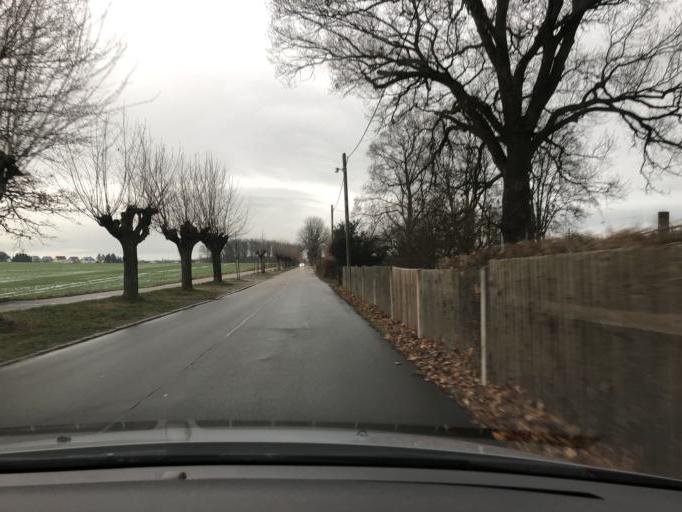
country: DE
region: Saxony
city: Limbach-Oberfrohna
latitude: 50.8606
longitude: 12.7312
